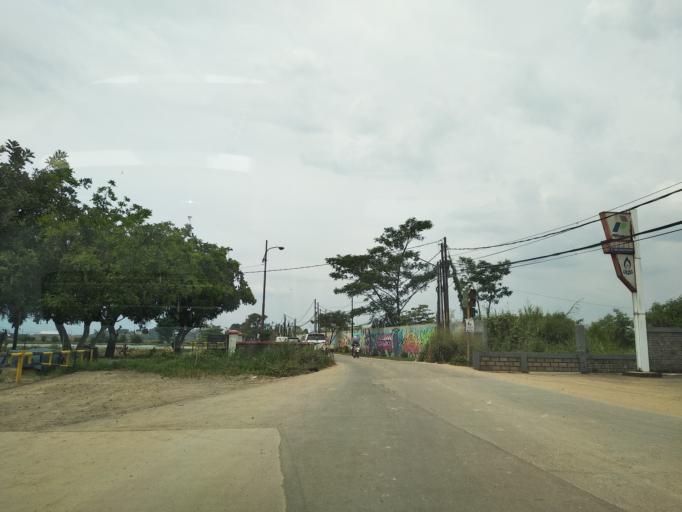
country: ID
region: West Java
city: Pameungpeuk
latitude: -6.9705
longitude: 107.6404
